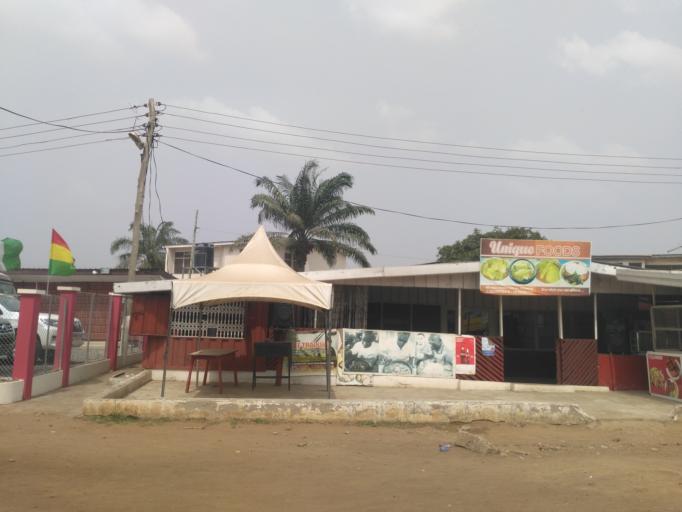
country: GH
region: Greater Accra
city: Nungua
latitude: 5.5937
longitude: -0.0891
